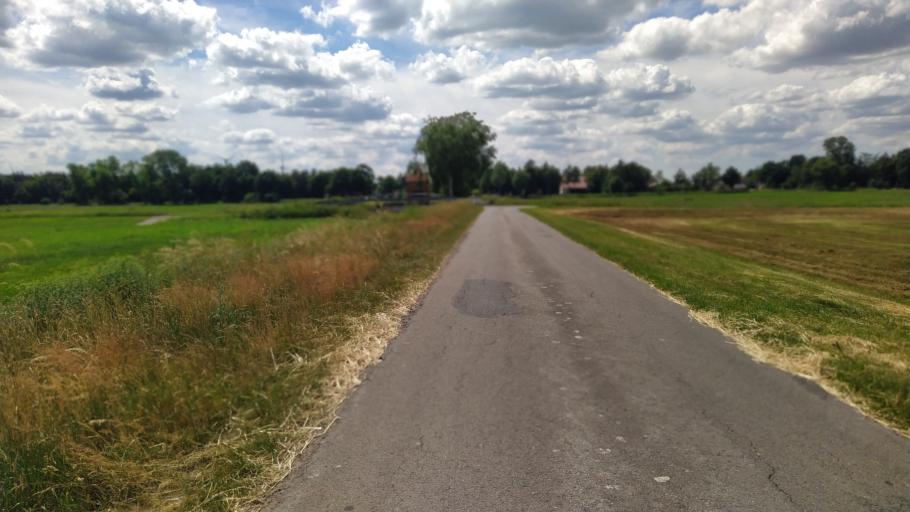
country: DE
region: Lower Saxony
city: Estorf
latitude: 53.5736
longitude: 9.1556
